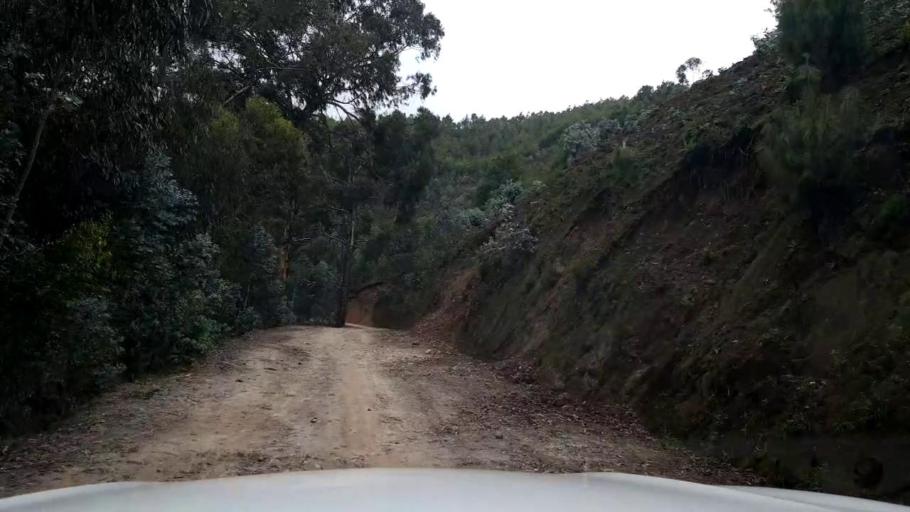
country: RW
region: Western Province
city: Kibuye
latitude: -1.9579
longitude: 29.4773
